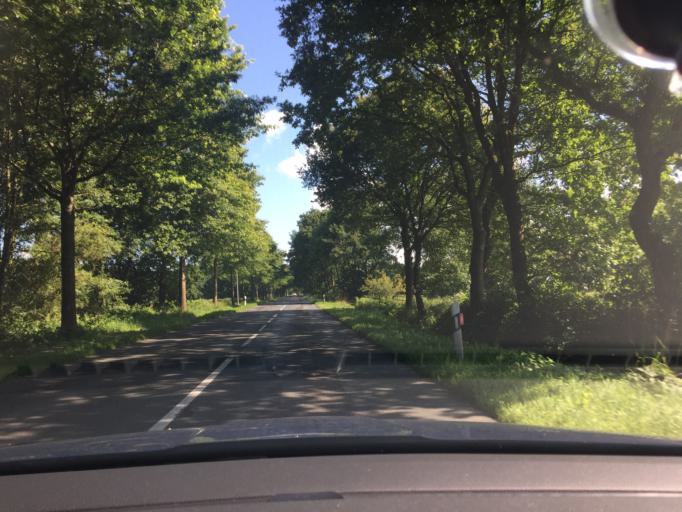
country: DE
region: Lower Saxony
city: Aurich
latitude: 53.4496
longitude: 7.4795
